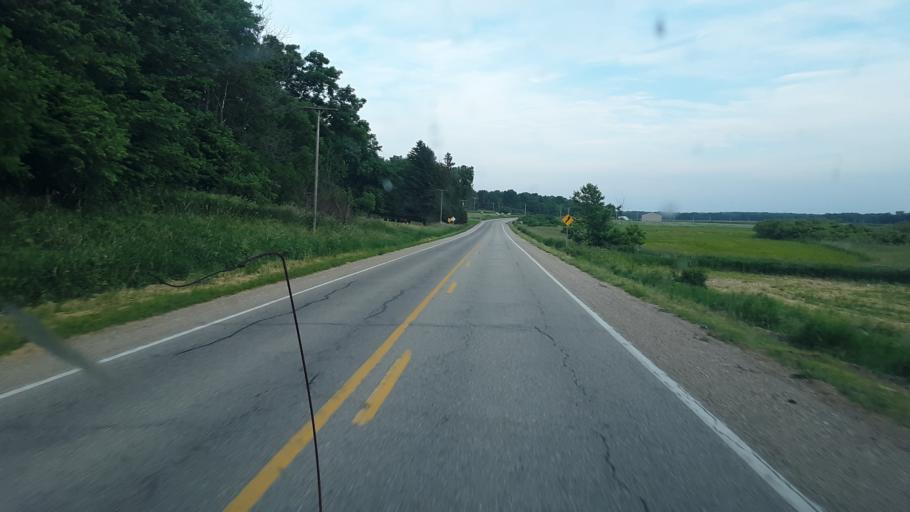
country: US
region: Iowa
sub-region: Benton County
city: Belle Plaine
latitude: 41.9499
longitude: -92.4198
